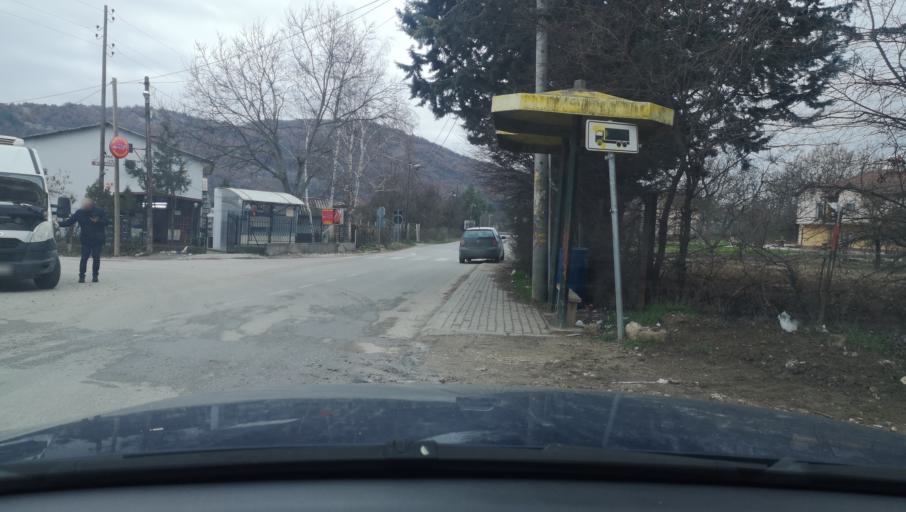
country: MK
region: Zelenikovo
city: Zelenikovo
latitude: 41.8985
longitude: 21.6020
